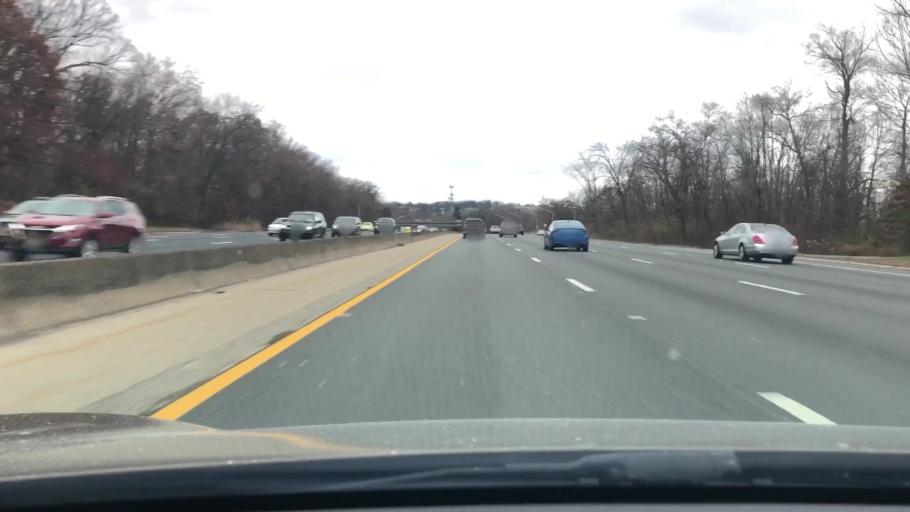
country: US
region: New Jersey
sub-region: Passaic County
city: Singac
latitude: 40.8982
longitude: -74.2285
